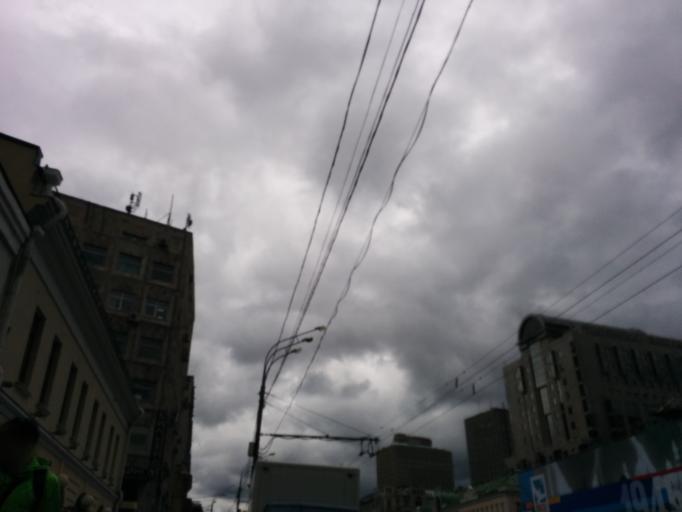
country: RU
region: Moskovskaya
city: Dorogomilovo
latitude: 55.7488
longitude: 37.5830
